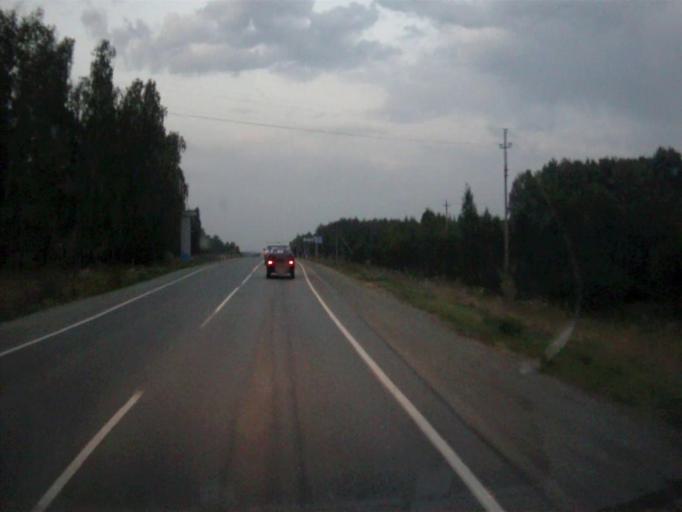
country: RU
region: Chelyabinsk
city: Timiryazevskiy
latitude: 55.2051
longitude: 60.7791
